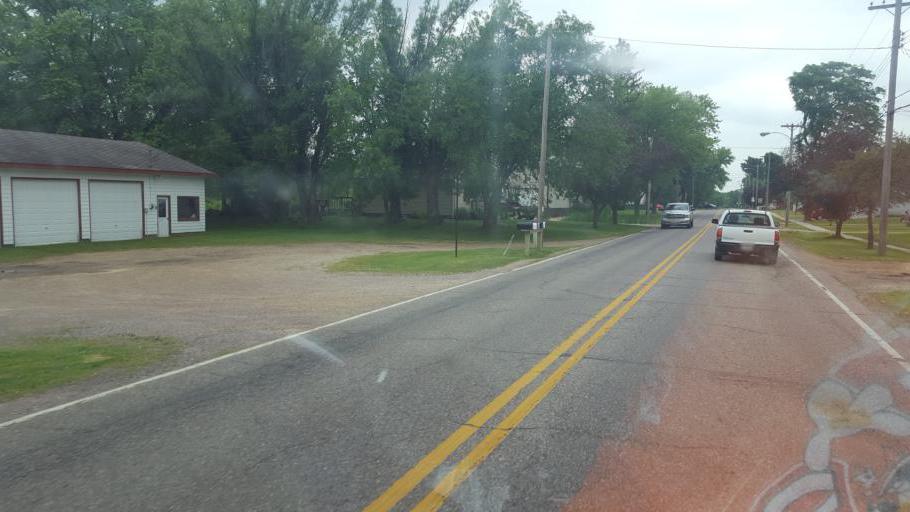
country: US
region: Wisconsin
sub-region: Juneau County
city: Elroy
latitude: 43.6444
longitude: -90.2187
